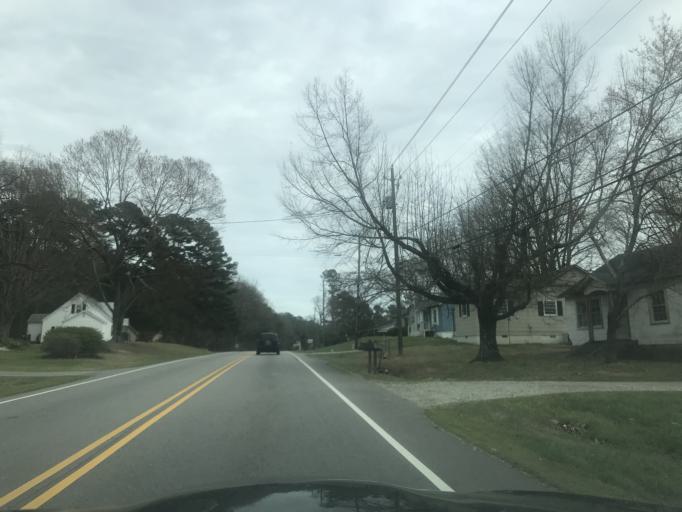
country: US
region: North Carolina
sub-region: Franklin County
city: Franklinton
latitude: 36.1022
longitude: -78.4320
